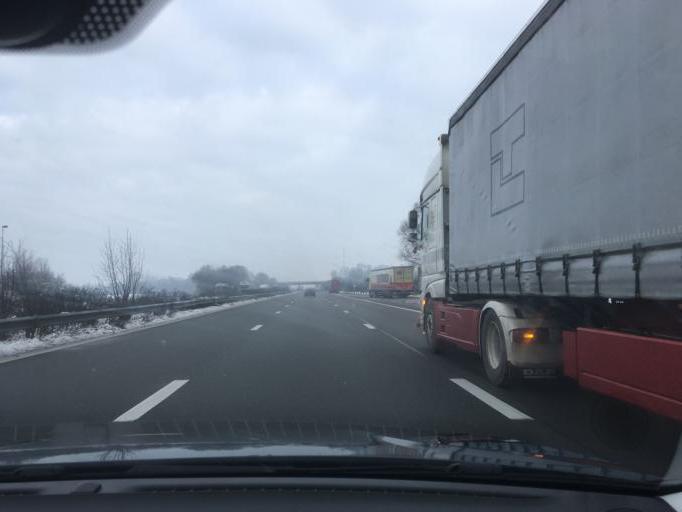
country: BE
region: Flanders
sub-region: Provincie West-Vlaanderen
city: Izegem
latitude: 50.8976
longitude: 3.1762
